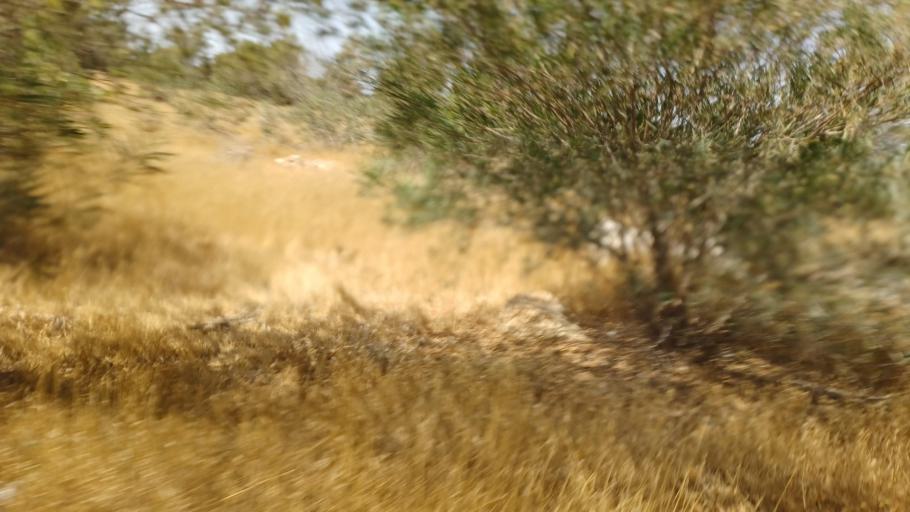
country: CY
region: Ammochostos
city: Paralimni
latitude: 35.0052
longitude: 33.9566
